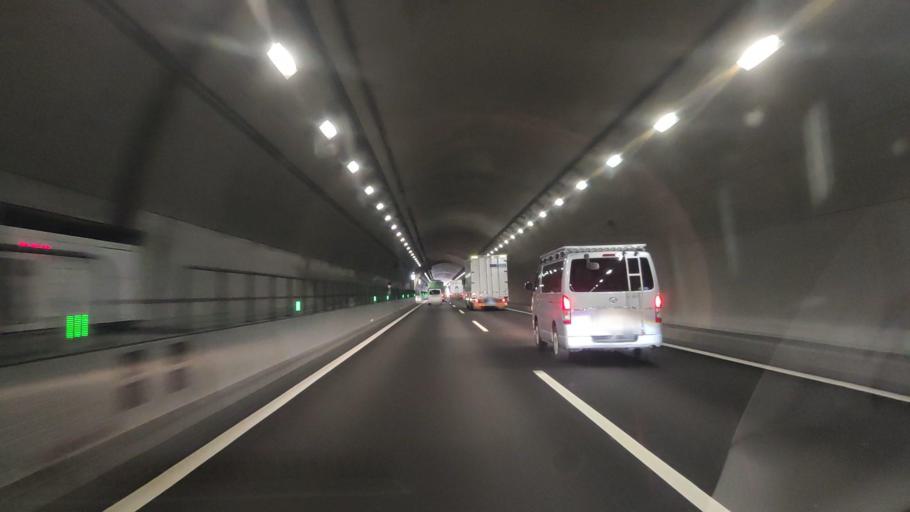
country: JP
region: Tokyo
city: Hachioji
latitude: 35.5633
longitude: 139.3100
